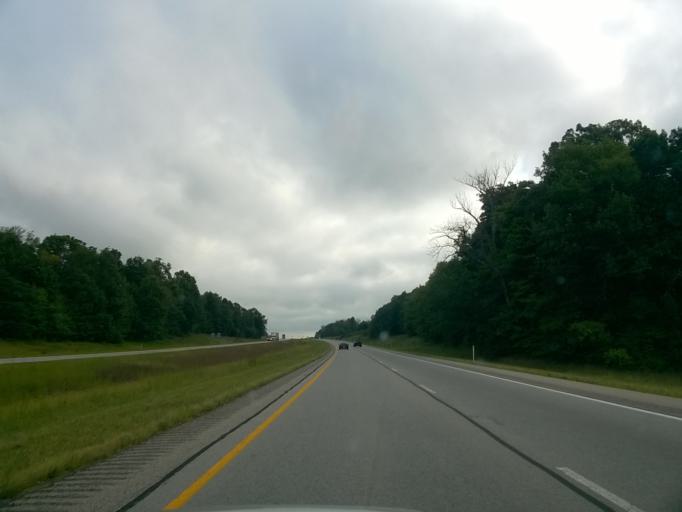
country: US
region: Indiana
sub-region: Floyd County
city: Georgetown
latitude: 38.2588
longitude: -86.0115
